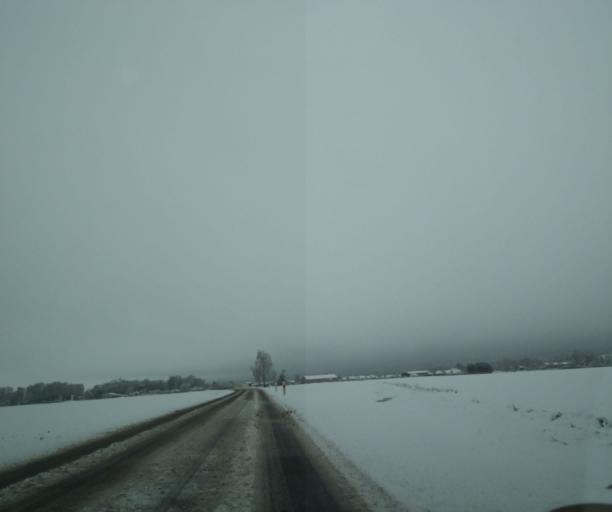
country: FR
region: Champagne-Ardenne
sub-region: Departement de la Haute-Marne
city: Wassy
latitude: 48.5535
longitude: 4.9261
